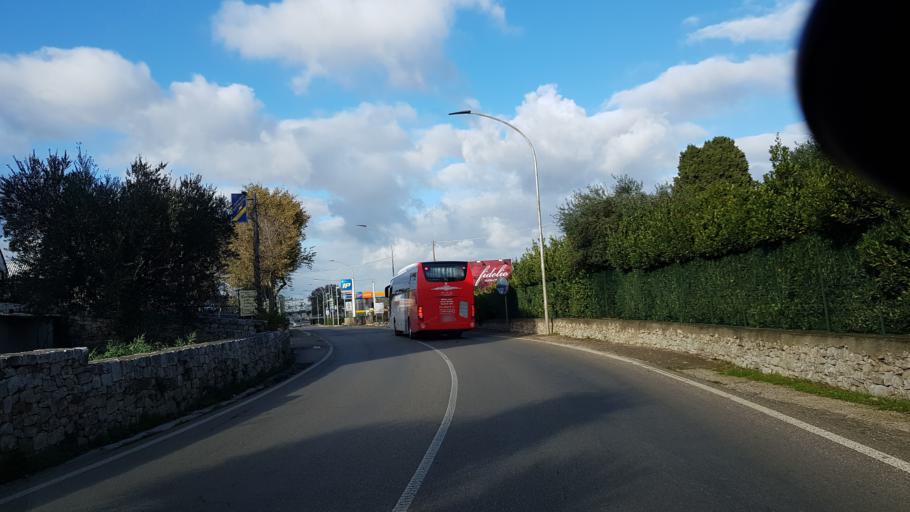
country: IT
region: Apulia
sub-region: Provincia di Bari
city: Alberobello
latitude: 40.7845
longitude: 17.2448
